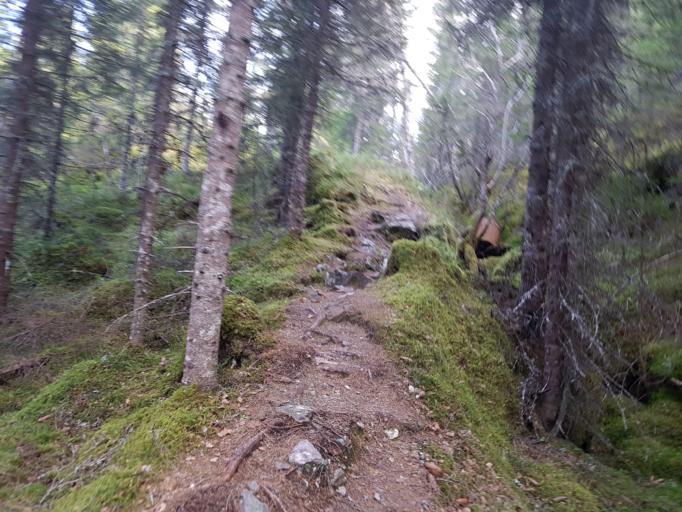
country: NO
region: Sor-Trondelag
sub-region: Trondheim
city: Trondheim
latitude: 63.4402
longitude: 10.2895
